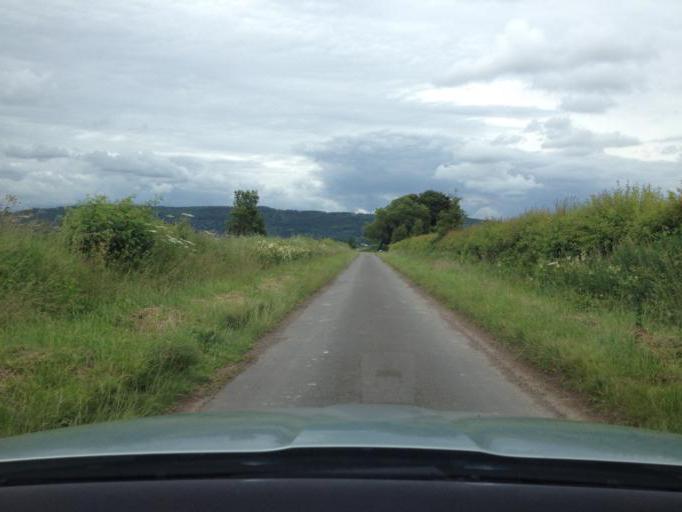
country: GB
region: Scotland
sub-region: Perth and Kinross
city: Bridge of Earn
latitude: 56.3311
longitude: -3.3911
